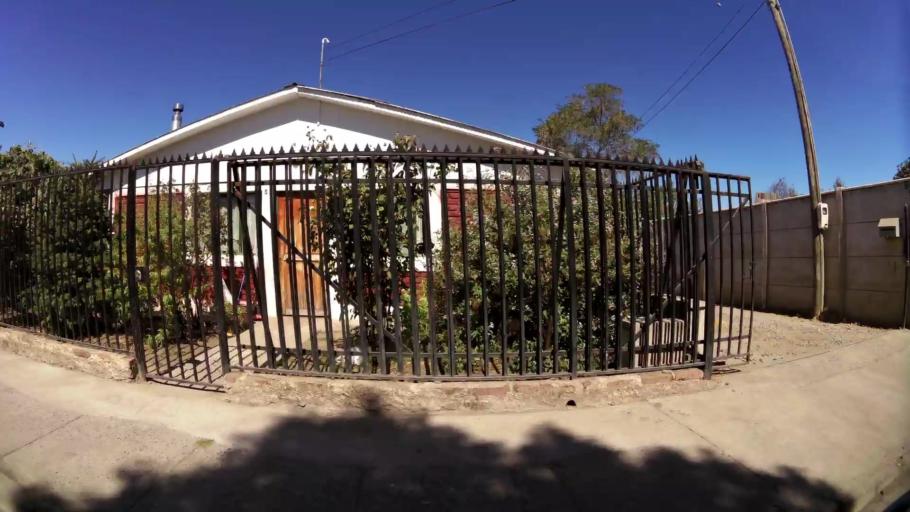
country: CL
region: O'Higgins
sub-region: Provincia de Colchagua
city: Chimbarongo
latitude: -34.5900
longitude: -70.9999
